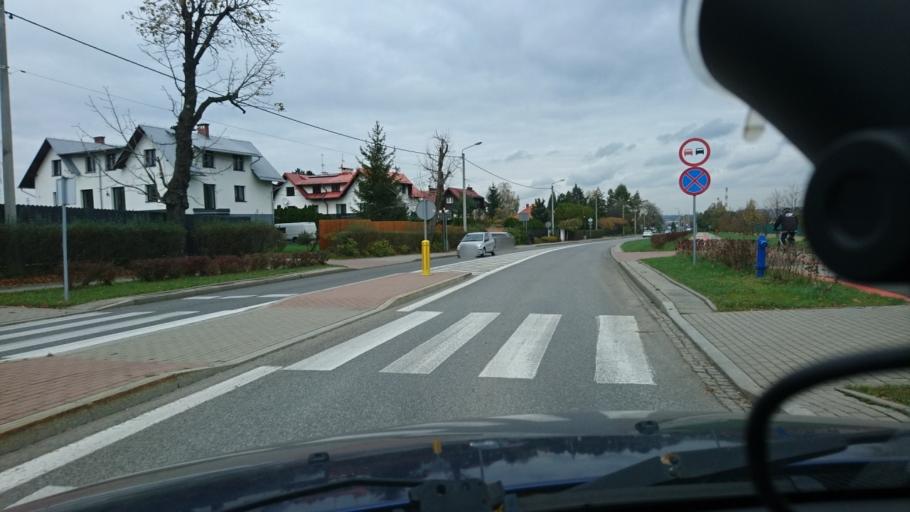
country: PL
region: Silesian Voivodeship
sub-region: Bielsko-Biala
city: Bielsko-Biala
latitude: 49.7904
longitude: 19.0356
